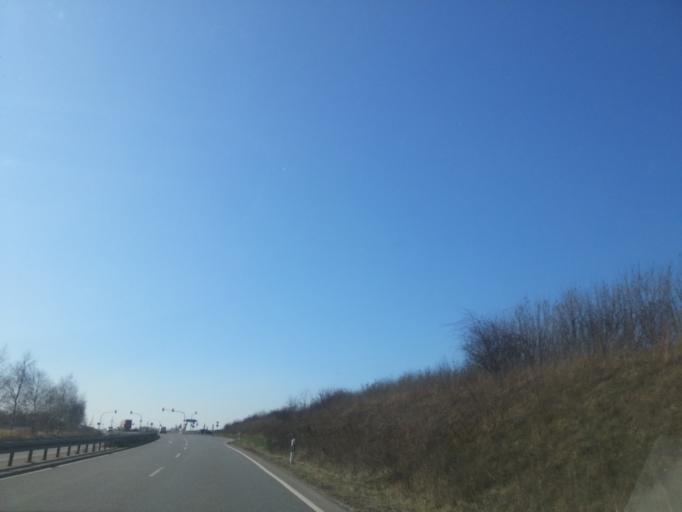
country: DE
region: Saxony
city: Freital
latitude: 51.0388
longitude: 13.6174
